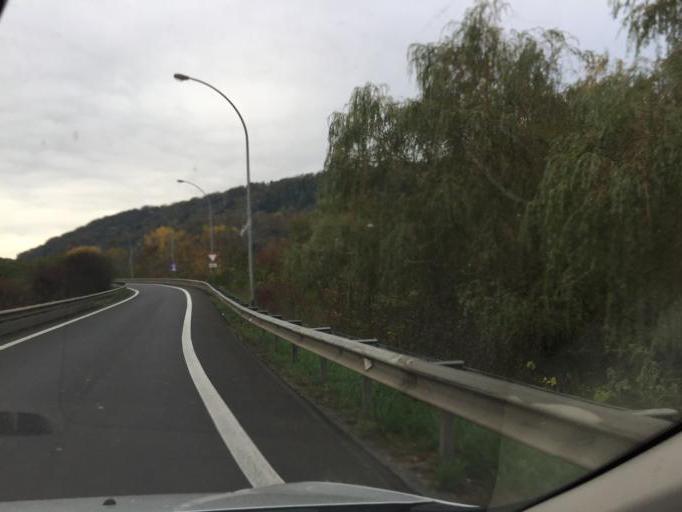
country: LU
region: Luxembourg
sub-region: Canton de Mersch
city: Mersch
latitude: 49.7386
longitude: 6.0968
